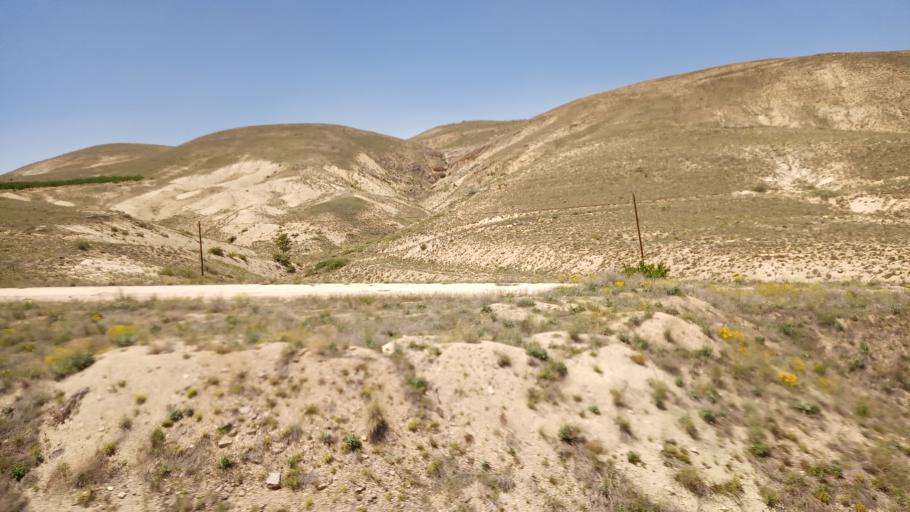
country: TR
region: Malatya
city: Darende
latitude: 38.6571
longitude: 37.4440
